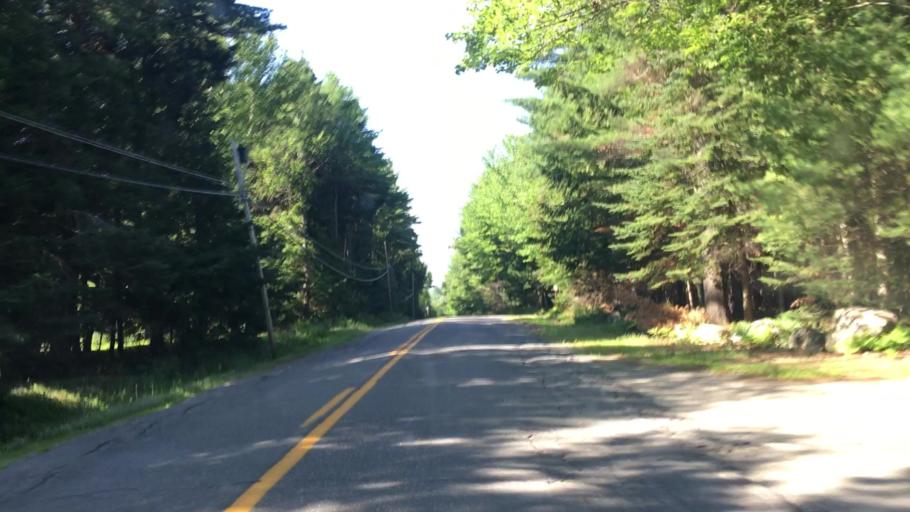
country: US
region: Maine
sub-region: Penobscot County
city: Enfield
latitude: 45.2637
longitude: -68.5625
